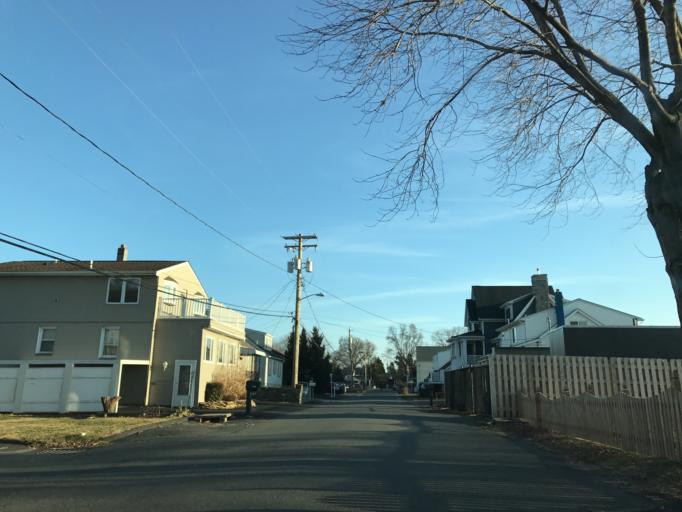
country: US
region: Maryland
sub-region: Baltimore County
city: Bowleys Quarters
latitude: 39.3113
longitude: -76.4134
